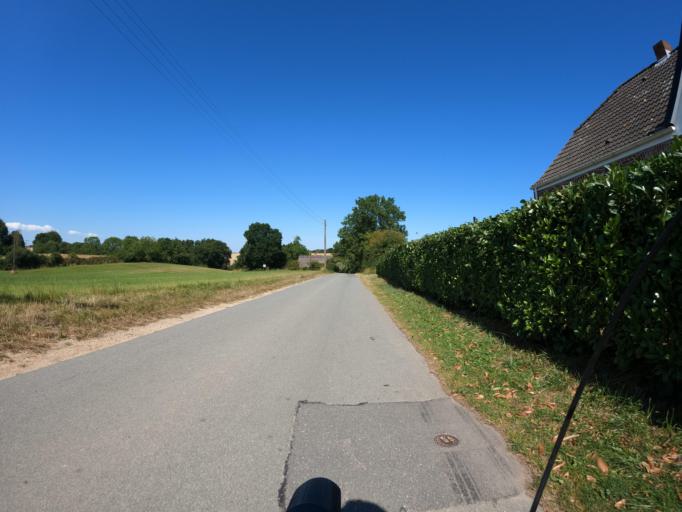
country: DE
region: Schleswig-Holstein
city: Steinbergkirche
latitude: 54.7911
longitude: 9.7450
